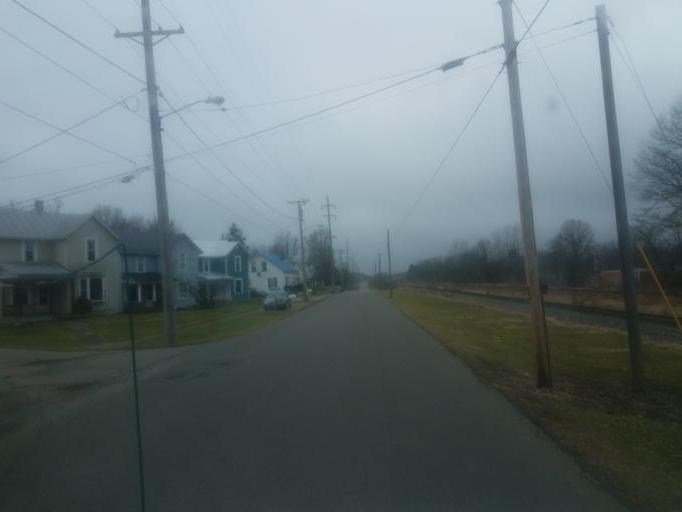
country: US
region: Ohio
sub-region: Crawford County
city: Galion
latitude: 40.7262
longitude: -82.7945
